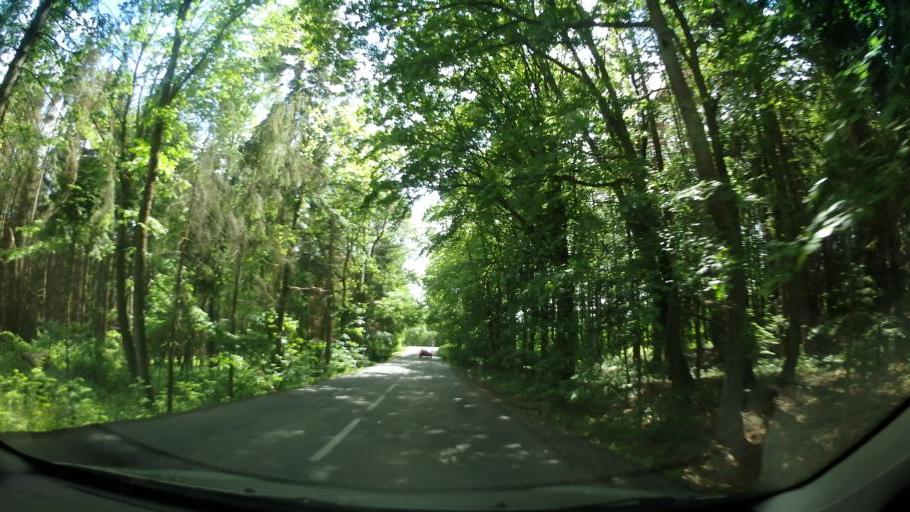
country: CZ
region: South Moravian
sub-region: Okres Blansko
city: Letovice
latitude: 49.5814
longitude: 16.5866
